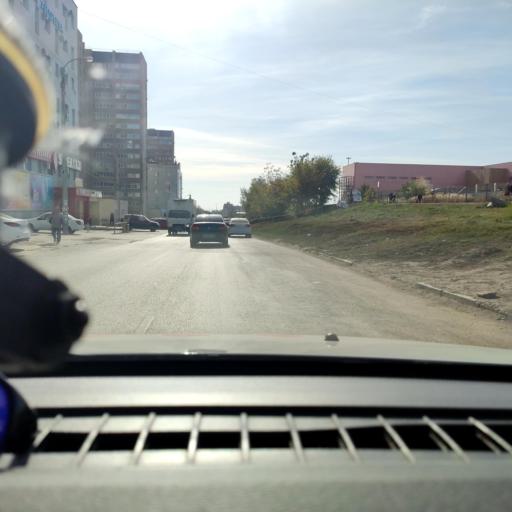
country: RU
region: Samara
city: Samara
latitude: 53.2093
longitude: 50.2029
